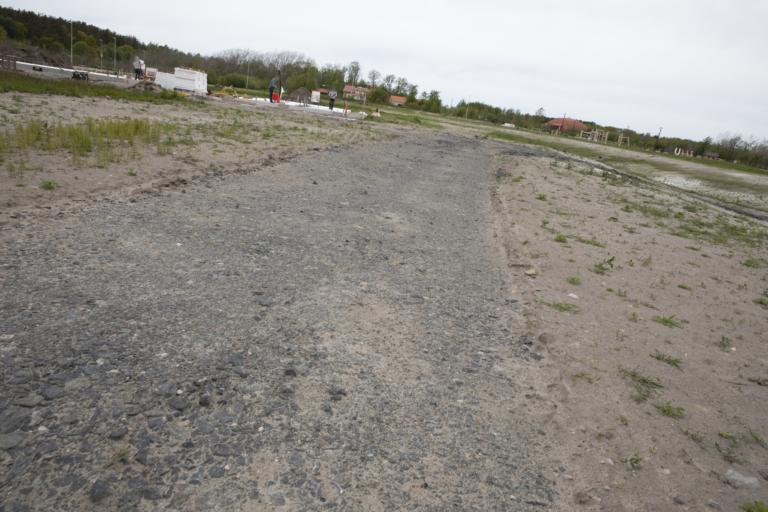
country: SE
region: Halland
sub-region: Varbergs Kommun
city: Varberg
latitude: 57.1469
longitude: 12.2355
